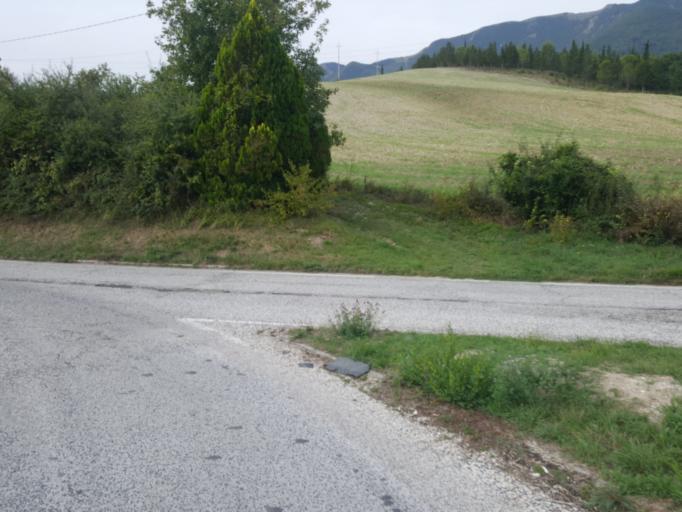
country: IT
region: The Marches
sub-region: Provincia di Ancona
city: Fabriano
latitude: 43.3506
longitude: 12.8294
